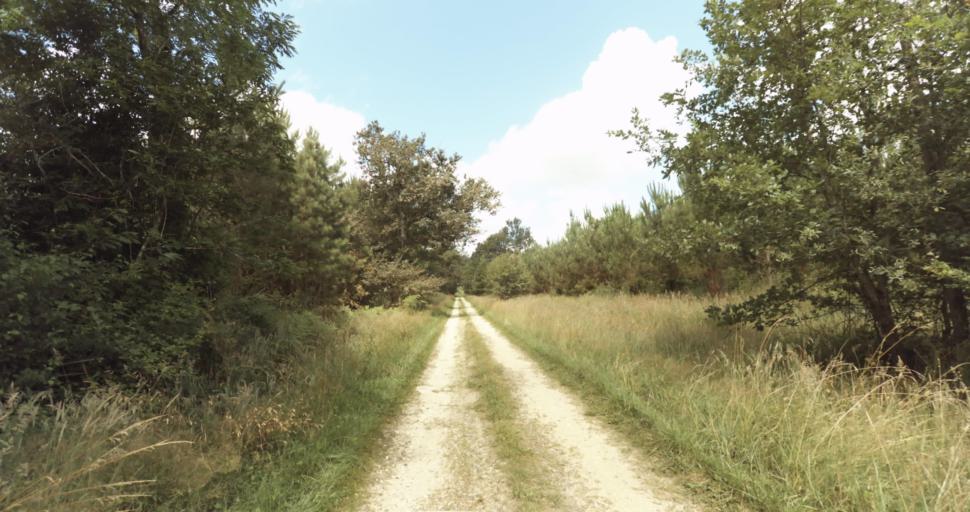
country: FR
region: Aquitaine
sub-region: Departement de la Gironde
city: Bazas
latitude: 44.4573
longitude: -0.1871
